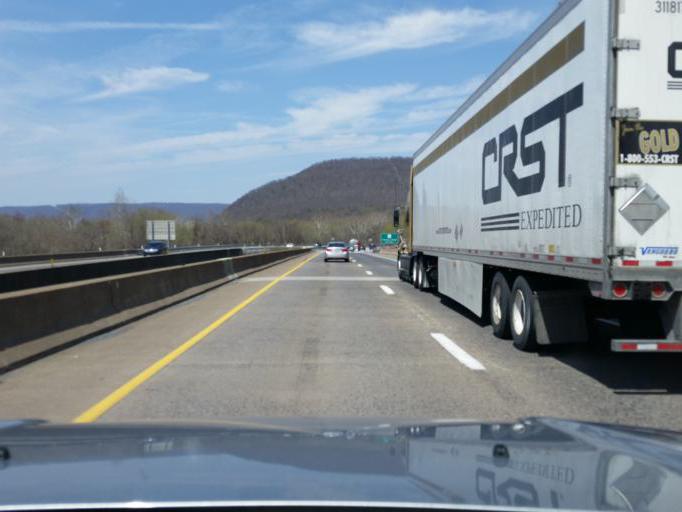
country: US
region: Pennsylvania
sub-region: Perry County
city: Marysville
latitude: 40.3395
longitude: -76.9044
